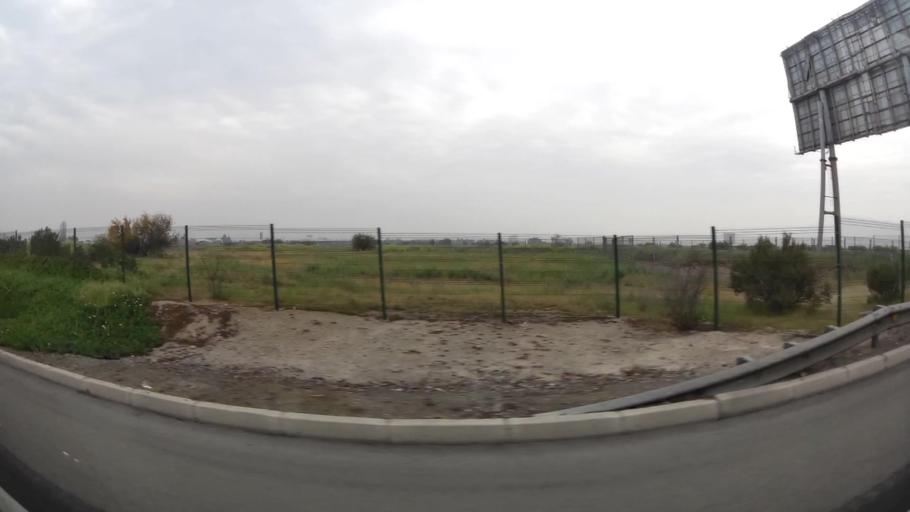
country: CL
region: Santiago Metropolitan
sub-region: Provincia de Santiago
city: Lo Prado
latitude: -33.4161
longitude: -70.7871
